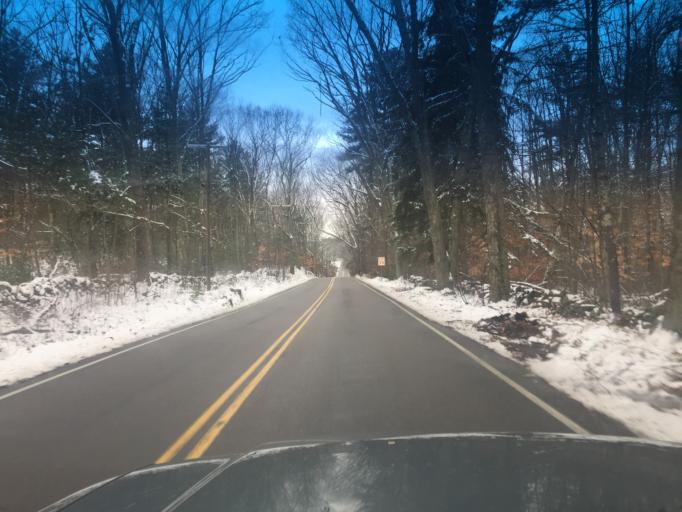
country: US
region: Massachusetts
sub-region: Middlesex County
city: Holliston
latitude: 42.1942
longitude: -71.3878
